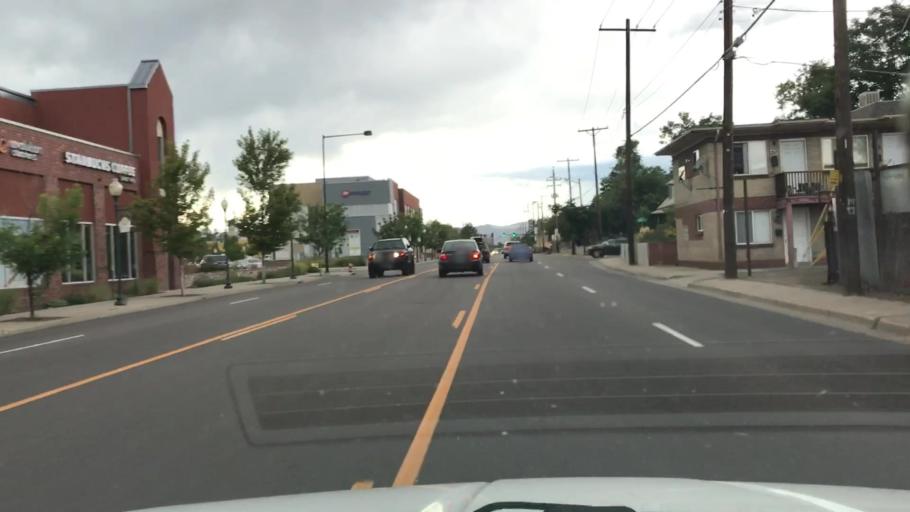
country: US
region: Colorado
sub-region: Jefferson County
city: Edgewater
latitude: 39.7694
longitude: -105.0454
